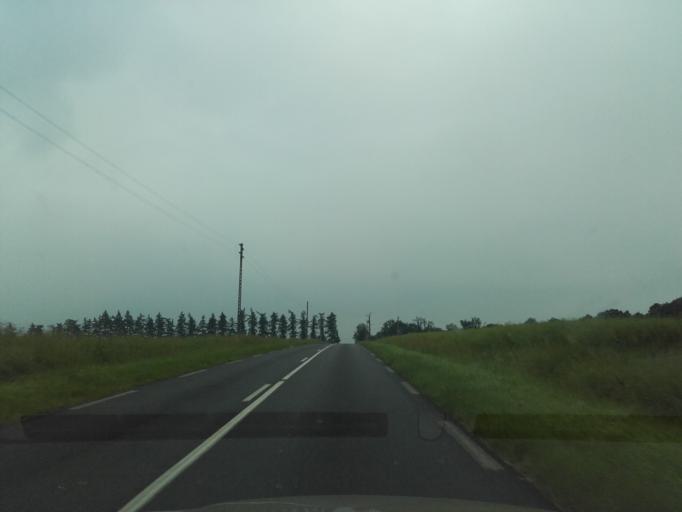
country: FR
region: Centre
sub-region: Departement d'Indre-et-Loire
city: Cerelles
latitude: 47.5304
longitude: 0.6930
